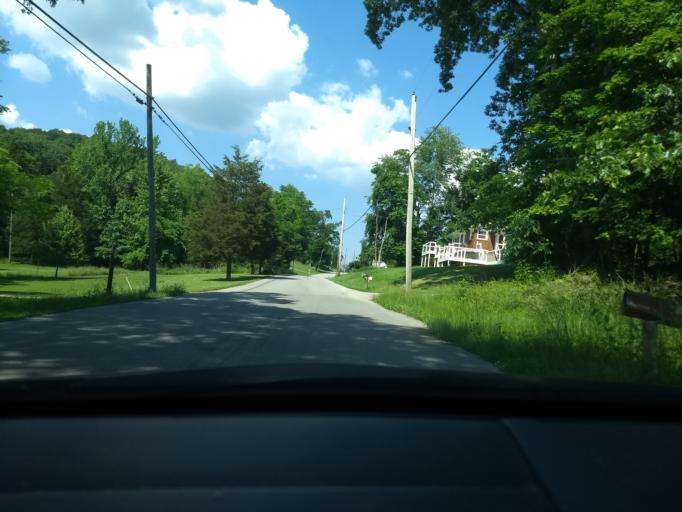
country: US
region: Indiana
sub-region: Floyd County
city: New Albany
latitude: 38.2635
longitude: -85.8595
